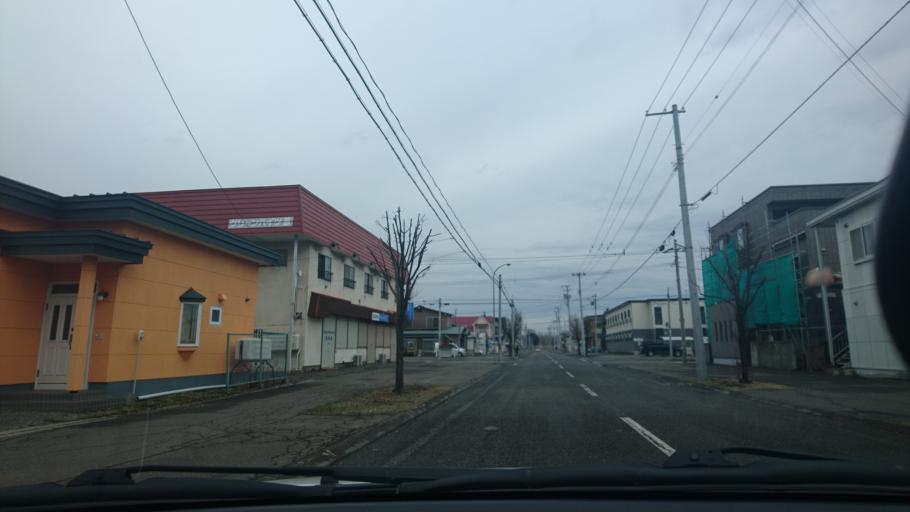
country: JP
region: Hokkaido
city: Obihiro
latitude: 42.9321
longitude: 143.1944
